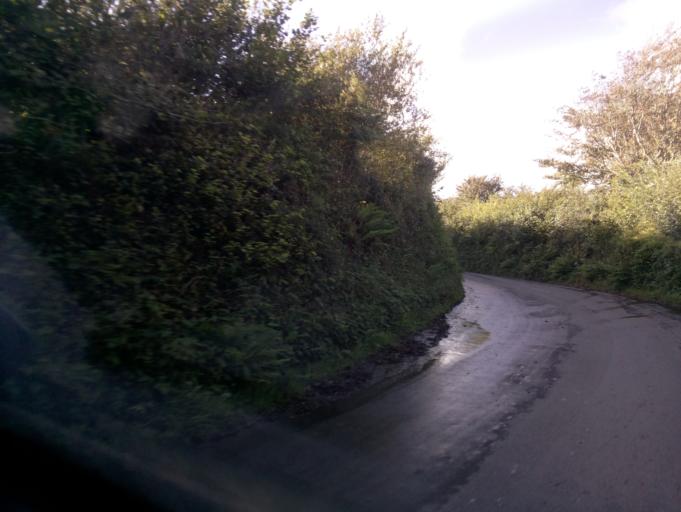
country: GB
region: England
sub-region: Devon
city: Totnes
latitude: 50.3491
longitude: -3.7151
